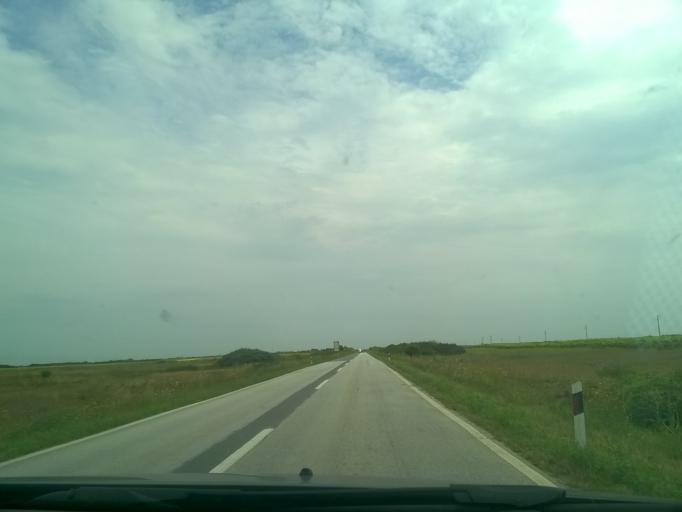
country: RS
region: Autonomna Pokrajina Vojvodina
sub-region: Srednjebanatski Okrug
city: Secanj
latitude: 45.3489
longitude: 20.7913
